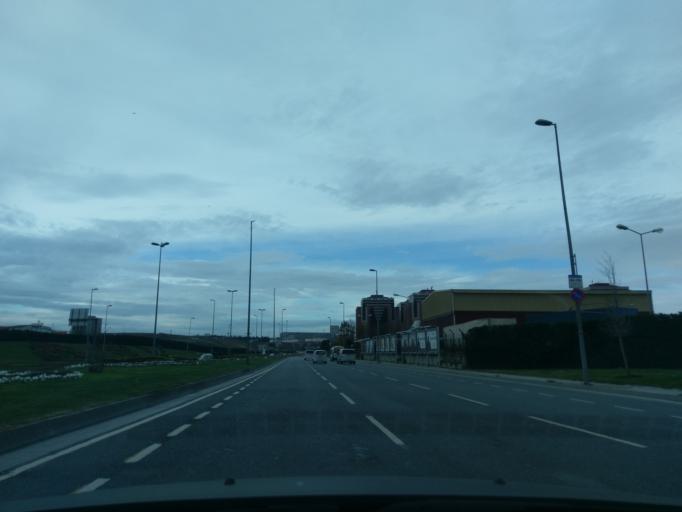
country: TR
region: Istanbul
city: Bahcelievler
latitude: 40.9830
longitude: 28.8375
